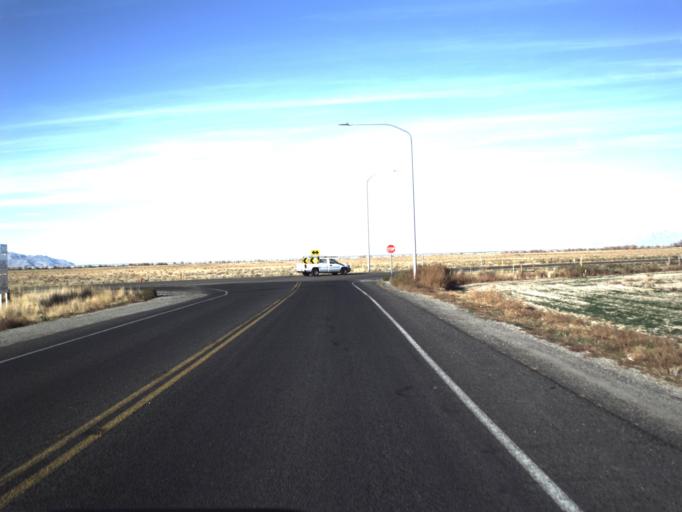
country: US
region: Utah
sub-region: Tooele County
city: Erda
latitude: 40.6135
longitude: -112.3710
